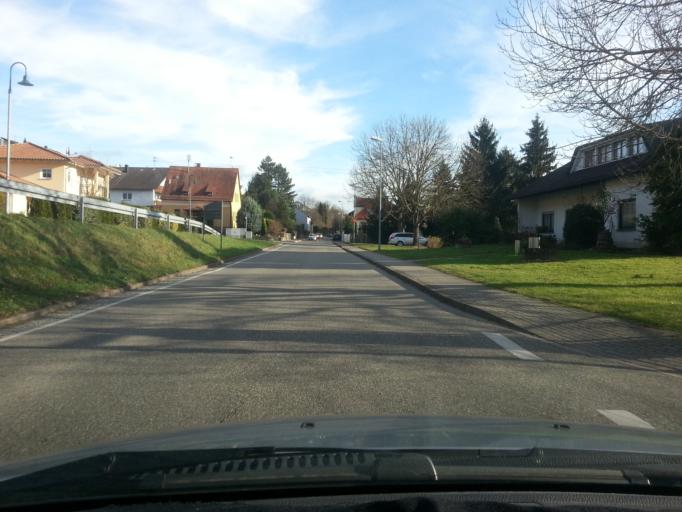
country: DE
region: Baden-Wuerttemberg
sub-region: Karlsruhe Region
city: Ostringen
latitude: 49.1810
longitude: 8.7408
